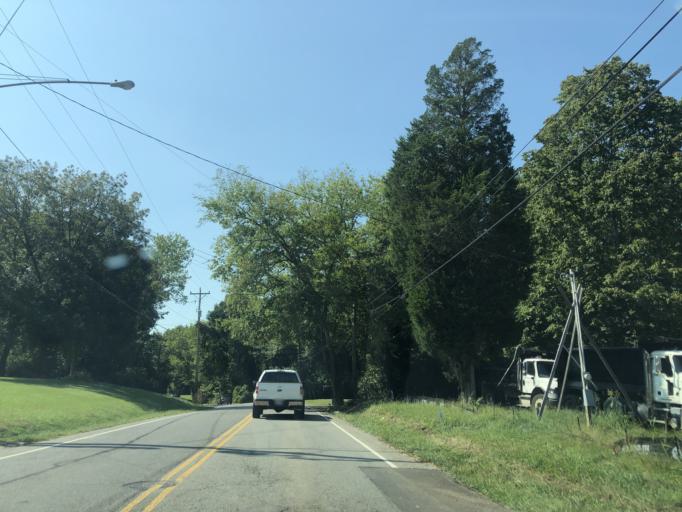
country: US
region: Tennessee
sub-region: Davidson County
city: Oak Hill
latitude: 36.0877
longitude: -86.7812
